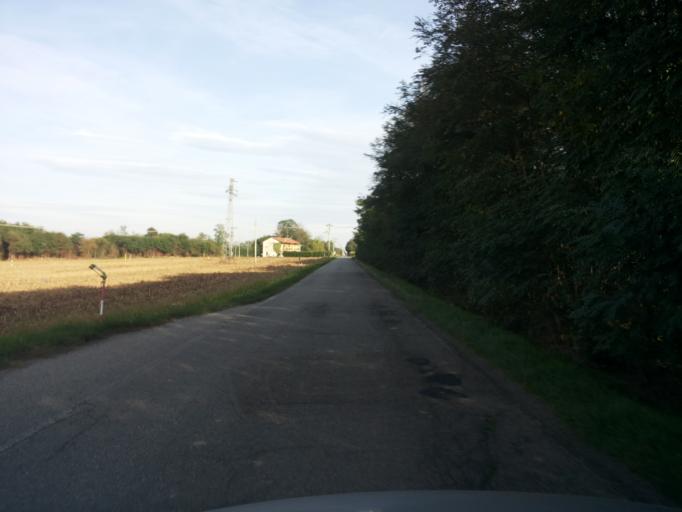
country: IT
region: Piedmont
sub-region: Provincia di Biella
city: Salussola
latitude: 45.4492
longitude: 8.1207
